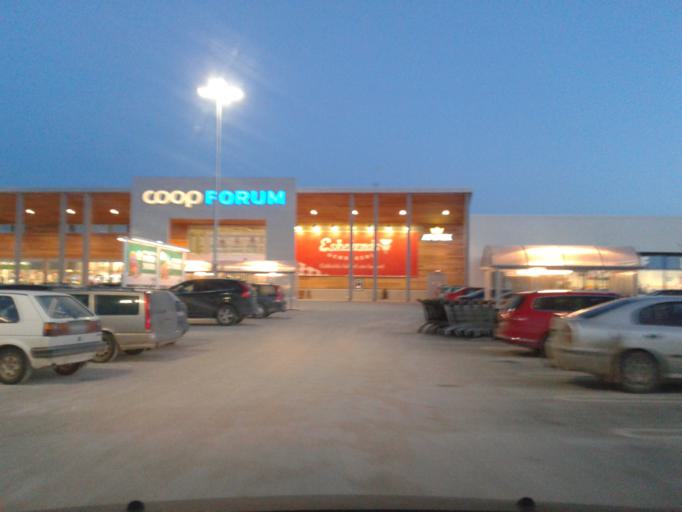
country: SE
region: Gotland
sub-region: Gotland
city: Visby
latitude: 57.6217
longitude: 18.3214
